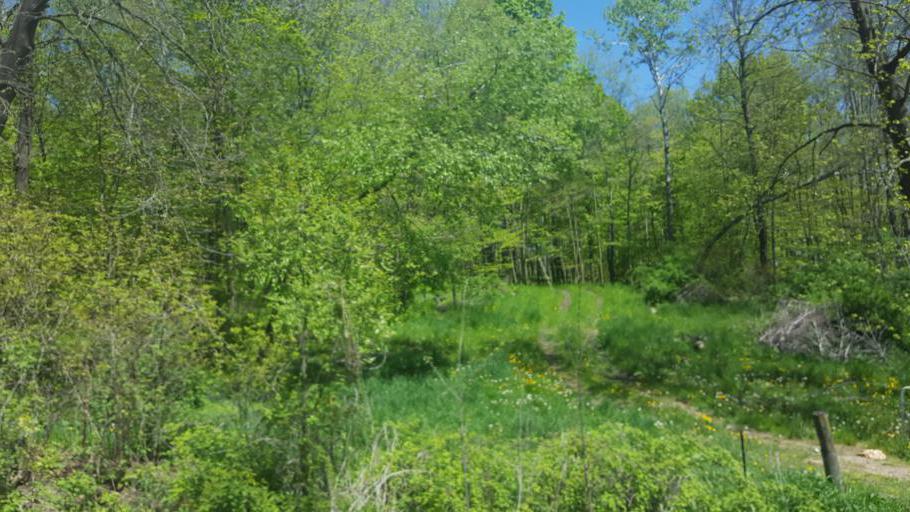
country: US
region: Wisconsin
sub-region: Vernon County
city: Hillsboro
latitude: 43.6431
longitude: -90.3656
